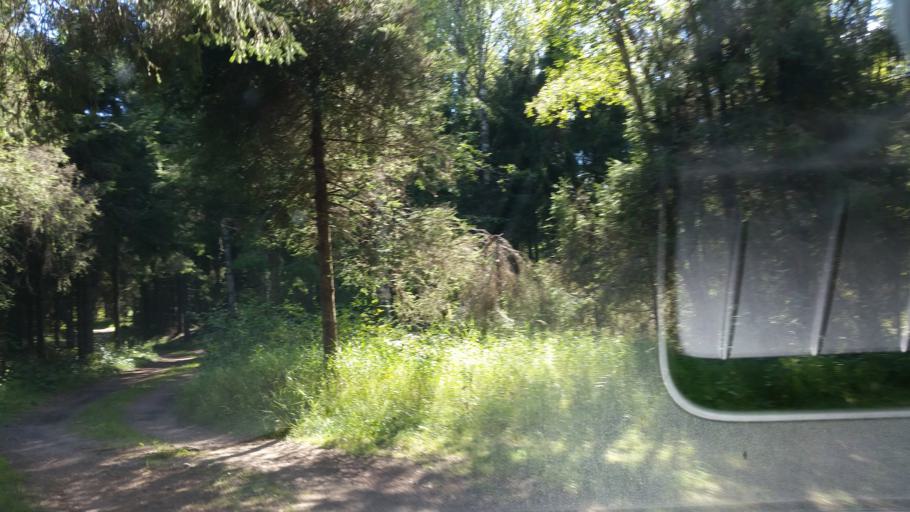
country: SE
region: Gaevleborg
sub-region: Ljusdals Kommun
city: Ljusdal
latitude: 61.9722
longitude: 16.3286
